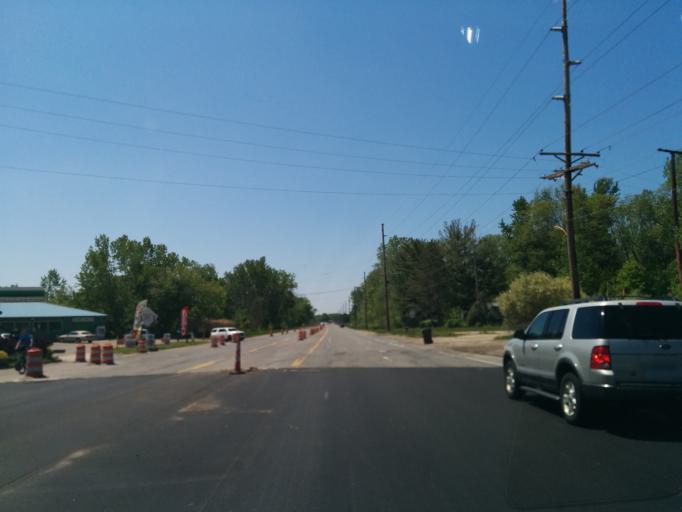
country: US
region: Michigan
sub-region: Berrien County
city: Bridgman
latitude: 41.9288
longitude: -86.5724
